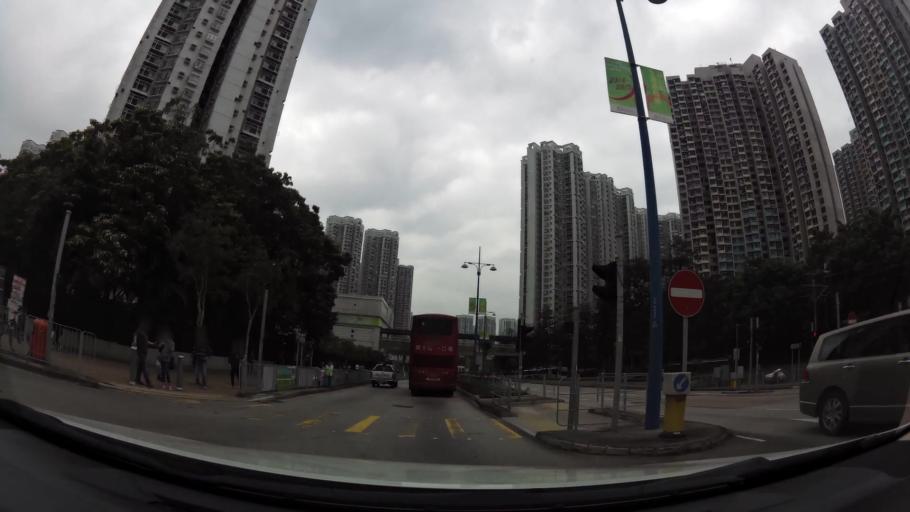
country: HK
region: Yuen Long
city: Yuen Long Kau Hui
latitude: 22.4509
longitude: 114.0021
